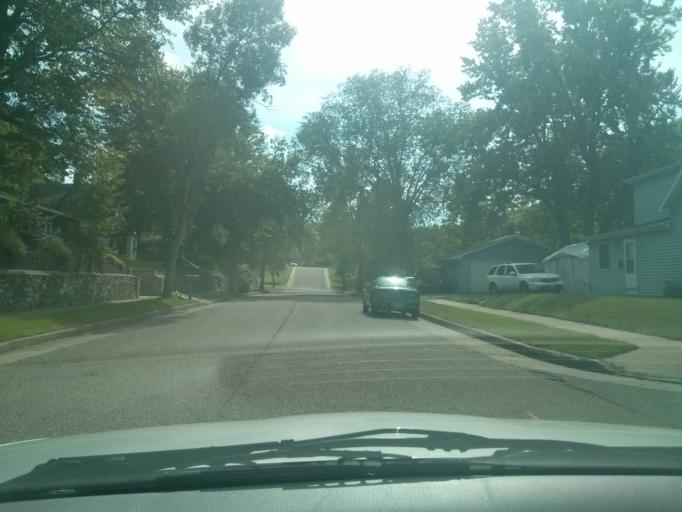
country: US
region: Wisconsin
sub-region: Saint Croix County
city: Hudson
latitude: 44.9787
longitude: -92.7452
